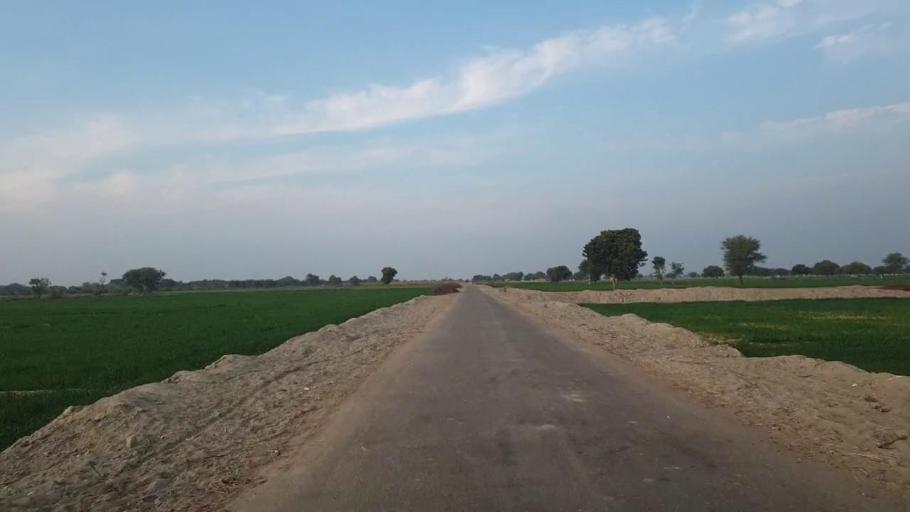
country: PK
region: Sindh
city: Shahpur Chakar
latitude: 26.1029
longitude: 68.5465
